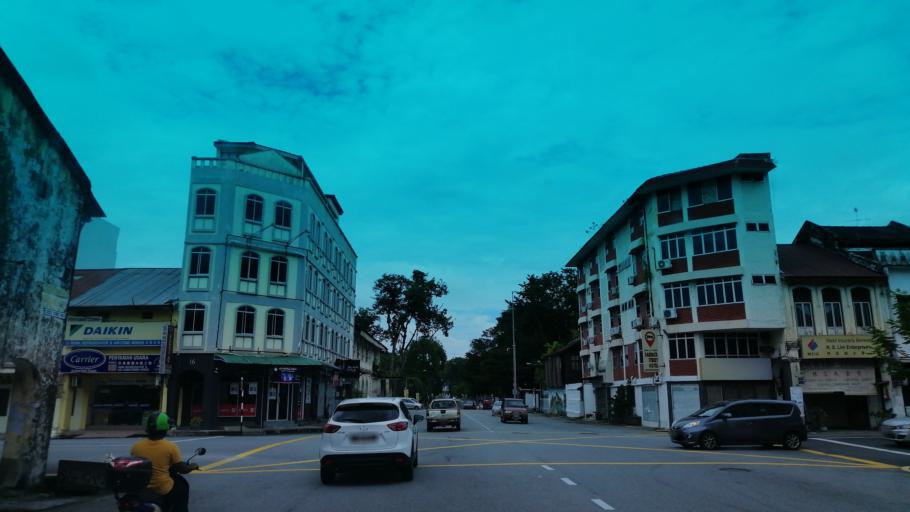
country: MY
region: Perak
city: Taiping
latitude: 4.8541
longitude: 100.7413
